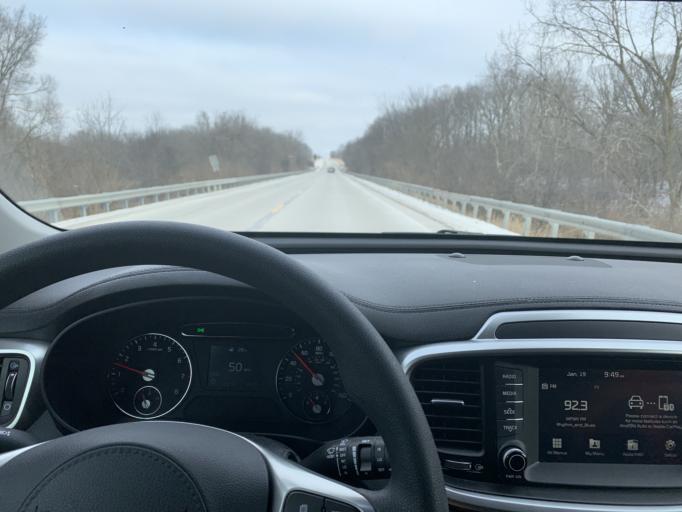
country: US
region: Illinois
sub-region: Will County
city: Fairmont
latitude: 41.5452
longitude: -88.0437
